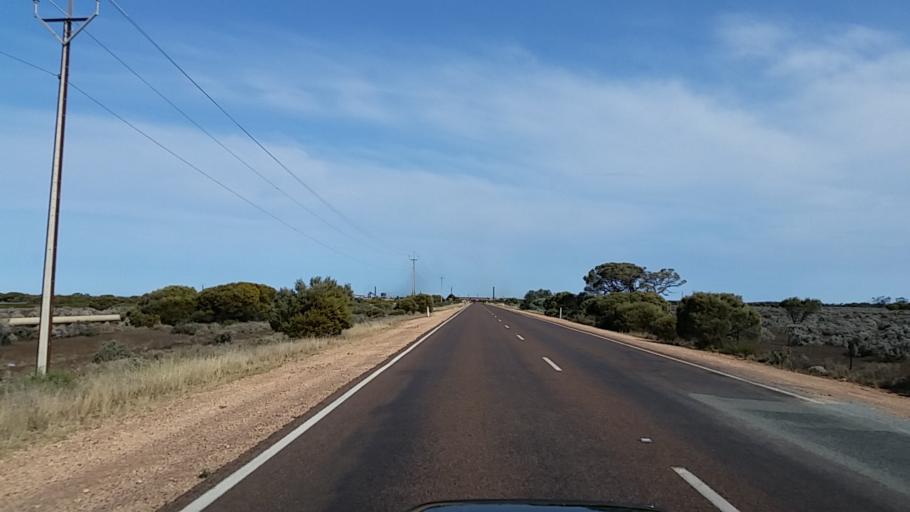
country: AU
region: South Australia
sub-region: Whyalla
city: Whyalla
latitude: -32.9724
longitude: 137.5795
